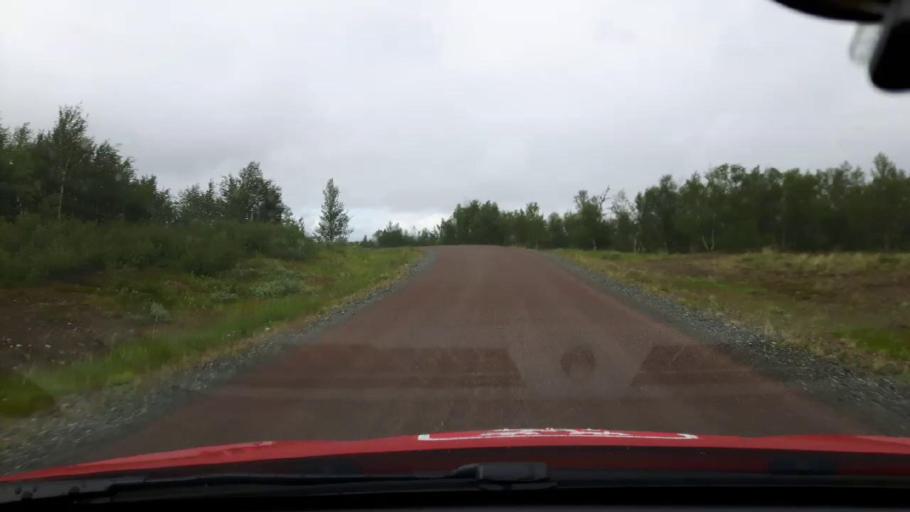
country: NO
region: Nord-Trondelag
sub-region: Meraker
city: Meraker
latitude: 63.2061
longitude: 12.4009
